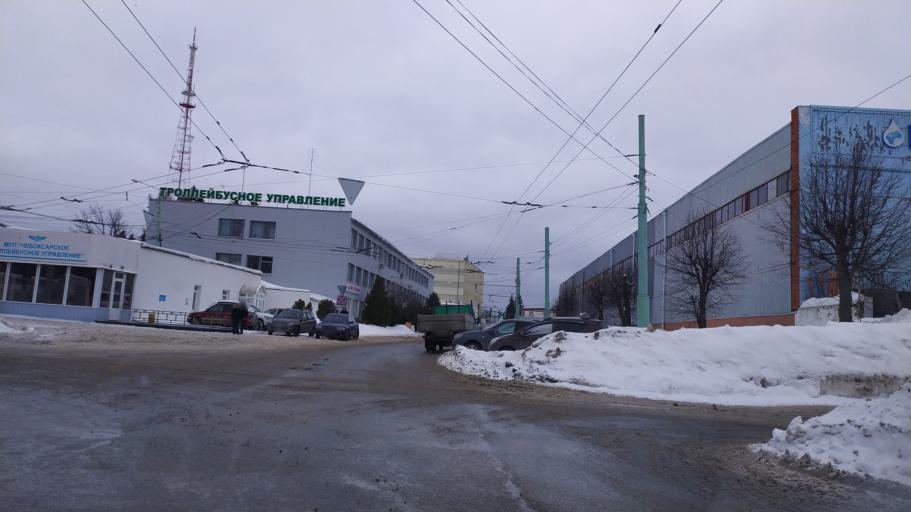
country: RU
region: Chuvashia
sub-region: Cheboksarskiy Rayon
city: Cheboksary
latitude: 56.1154
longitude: 47.2653
